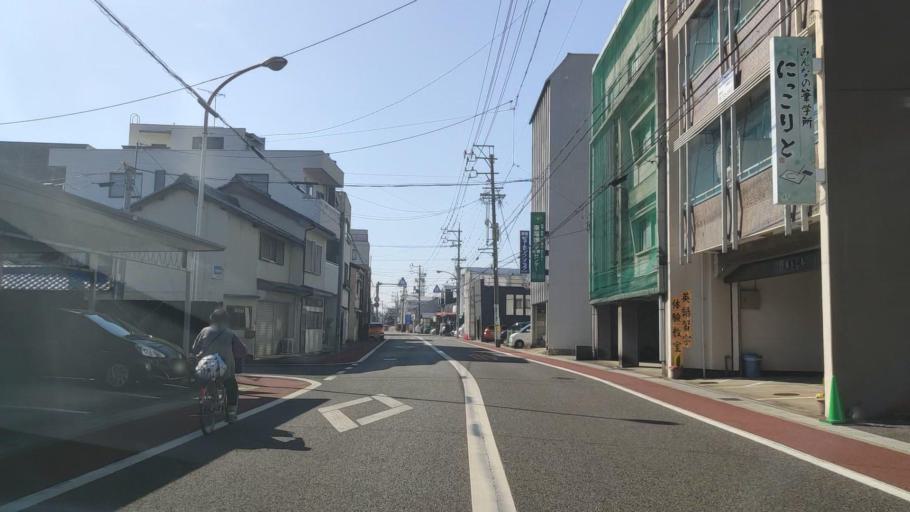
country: JP
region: Gifu
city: Gifu-shi
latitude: 35.4295
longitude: 136.7573
